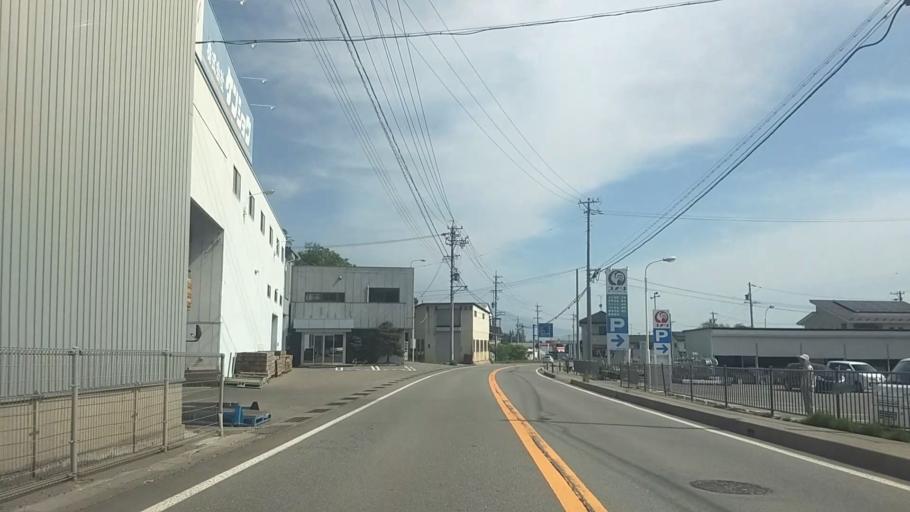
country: JP
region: Nagano
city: Saku
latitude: 36.1259
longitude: 138.4690
